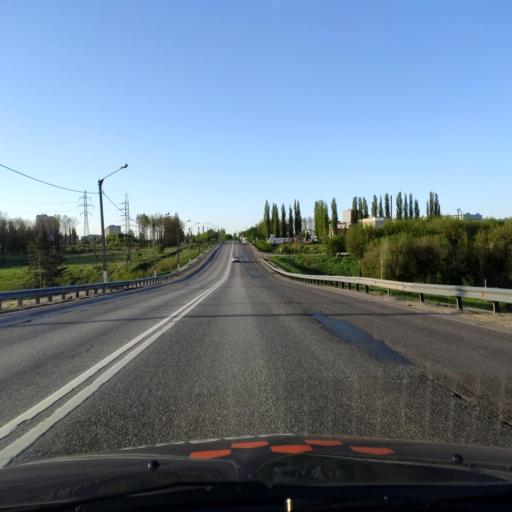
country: RU
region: Lipetsk
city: Yelets
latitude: 52.6163
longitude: 38.4606
